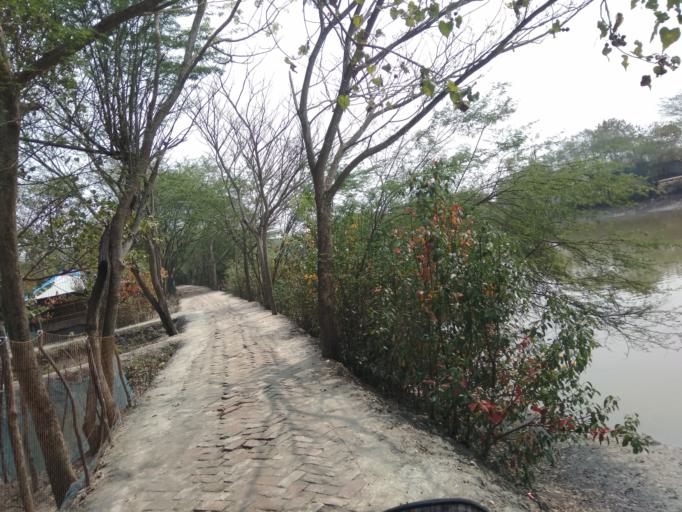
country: IN
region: West Bengal
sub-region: North 24 Parganas
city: Gosaba
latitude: 22.2562
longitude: 89.2535
